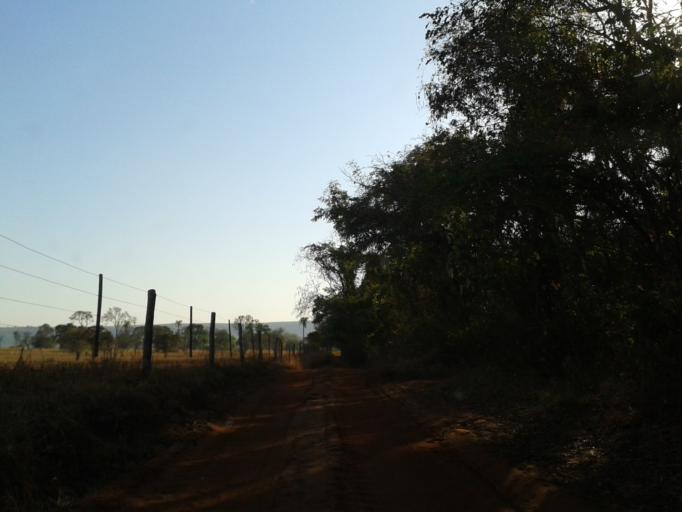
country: BR
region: Minas Gerais
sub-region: Santa Vitoria
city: Santa Vitoria
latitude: -19.1806
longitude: -50.0260
